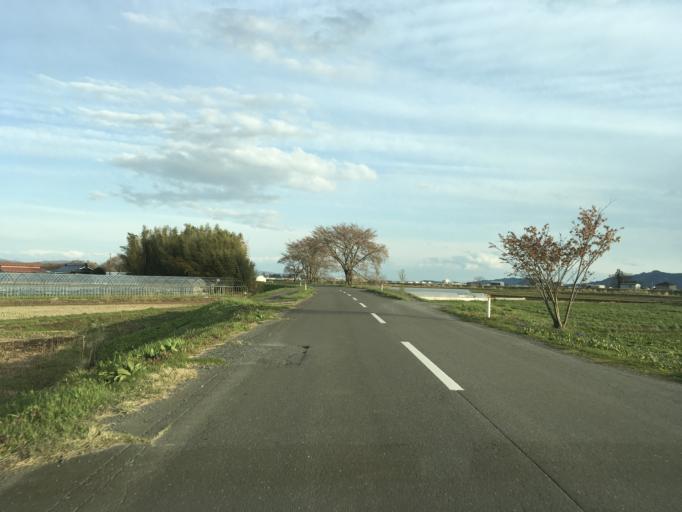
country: JP
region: Miyagi
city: Wakuya
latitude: 38.6453
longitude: 141.1788
